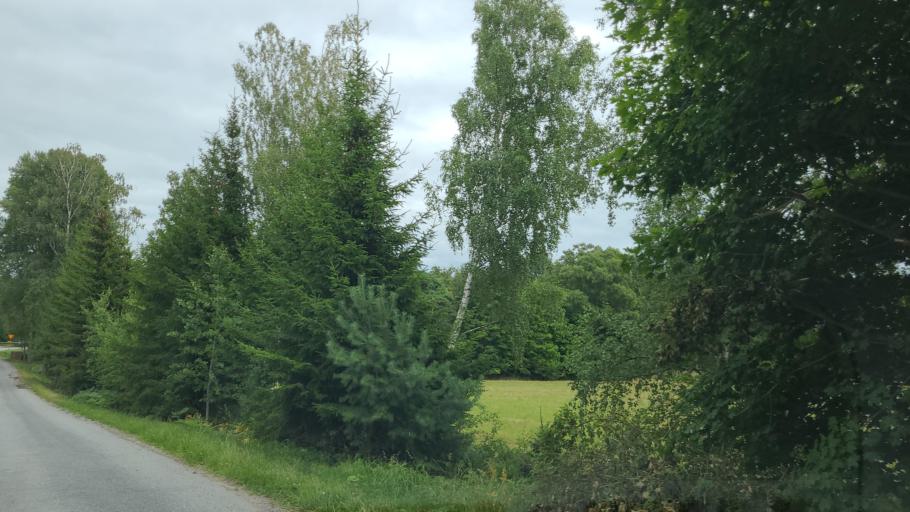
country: SE
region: Uppsala
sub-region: Habo Kommun
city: Balsta
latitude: 59.5393
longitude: 17.5644
